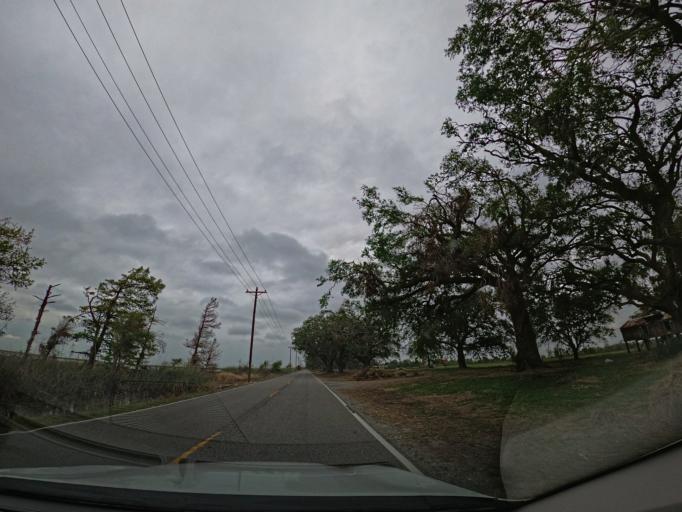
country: US
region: Louisiana
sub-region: Cameron Parish
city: Cameron
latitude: 29.7562
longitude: -92.9248
